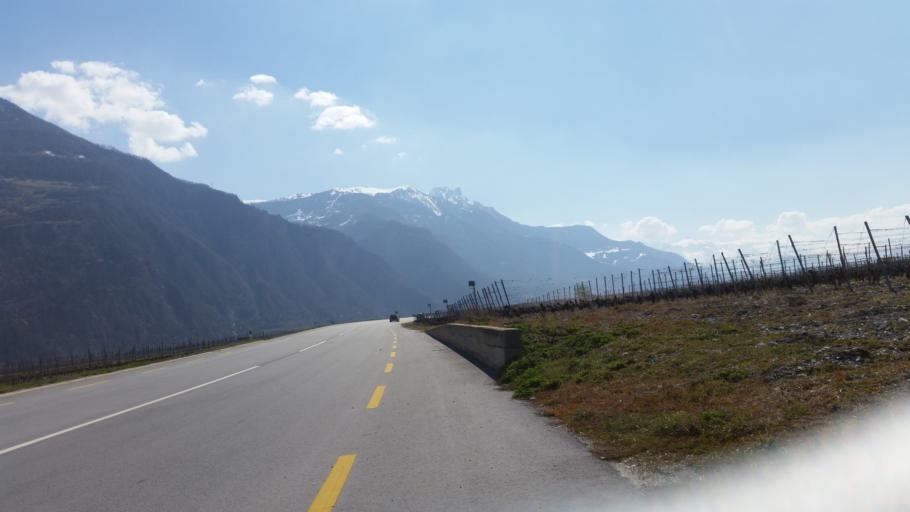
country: CH
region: Valais
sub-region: Conthey District
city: Ardon
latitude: 46.2019
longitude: 7.2482
